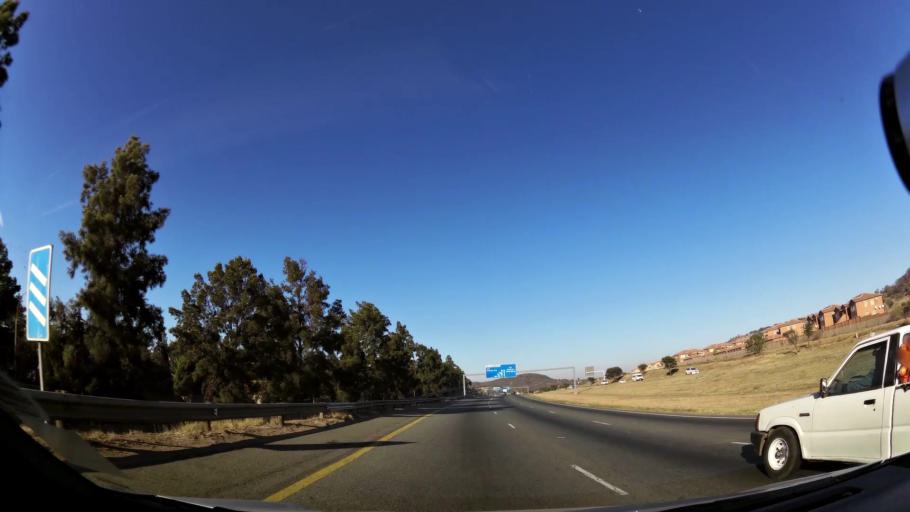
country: ZA
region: Gauteng
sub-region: Ekurhuleni Metropolitan Municipality
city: Germiston
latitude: -26.2789
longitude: 28.1039
